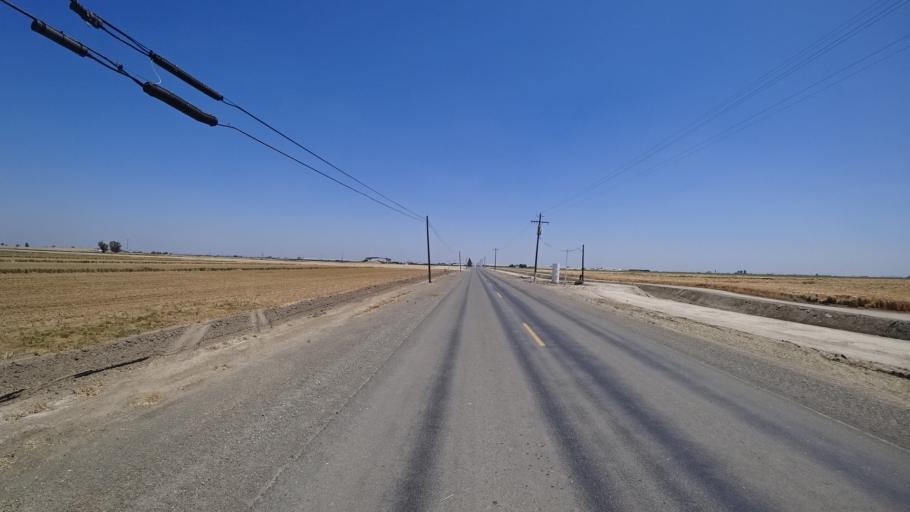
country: US
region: California
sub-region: Kings County
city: Home Garden
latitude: 36.1967
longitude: -119.6240
